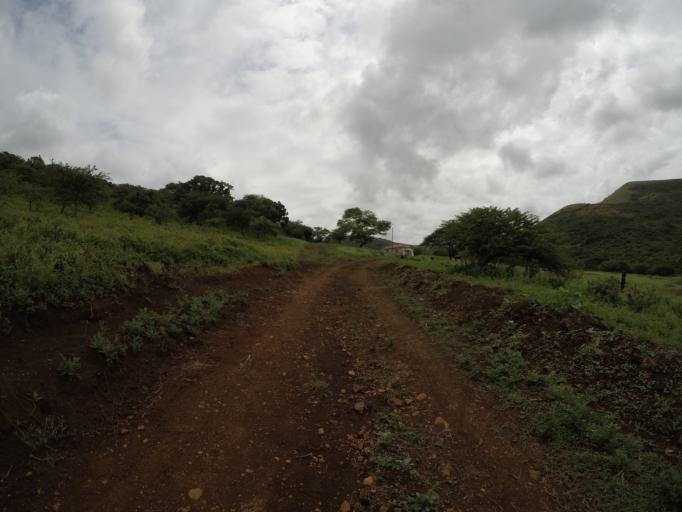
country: ZA
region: KwaZulu-Natal
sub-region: uThungulu District Municipality
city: Empangeni
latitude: -28.5807
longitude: 31.8890
